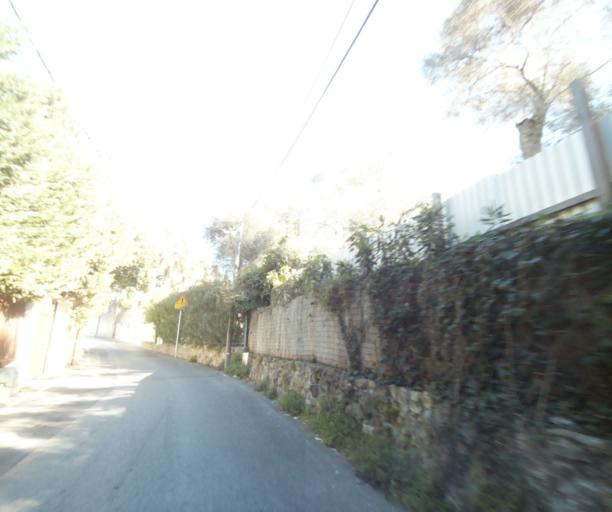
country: FR
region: Provence-Alpes-Cote d'Azur
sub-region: Departement des Alpes-Maritimes
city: Antibes
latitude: 43.5602
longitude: 7.1273
